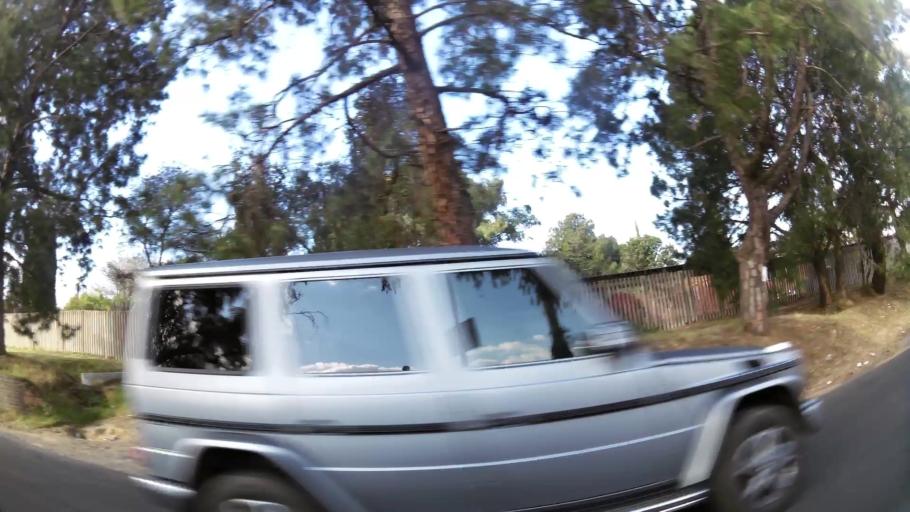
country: ZA
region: Gauteng
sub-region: City of Johannesburg Metropolitan Municipality
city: Midrand
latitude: -26.0048
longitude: 28.1254
